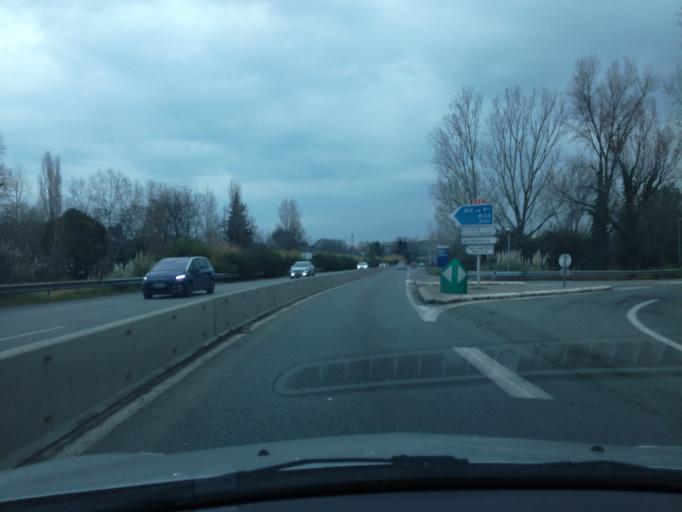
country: FR
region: Provence-Alpes-Cote d'Azur
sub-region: Departement des Alpes-Maritimes
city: Mandelieu-la-Napoule
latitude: 43.5605
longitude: 6.9538
